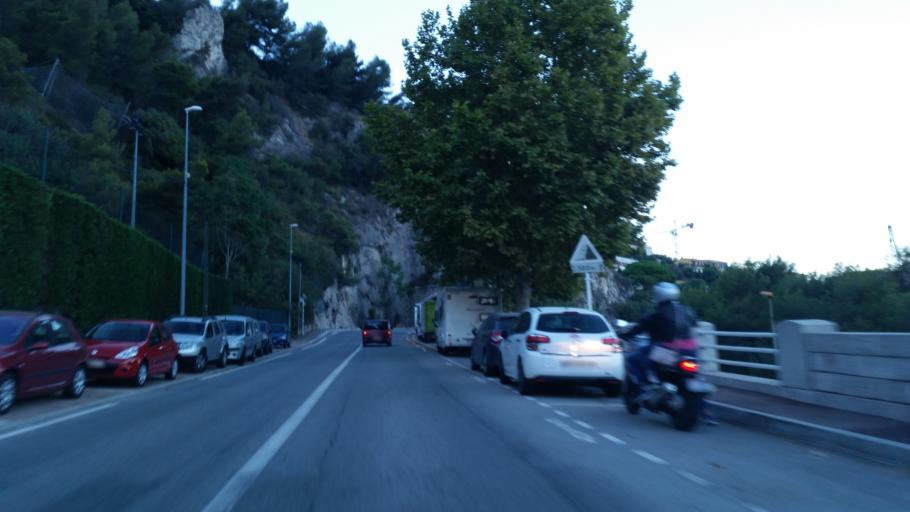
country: MC
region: Commune de Monaco
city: Monaco
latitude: 43.7301
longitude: 7.4090
